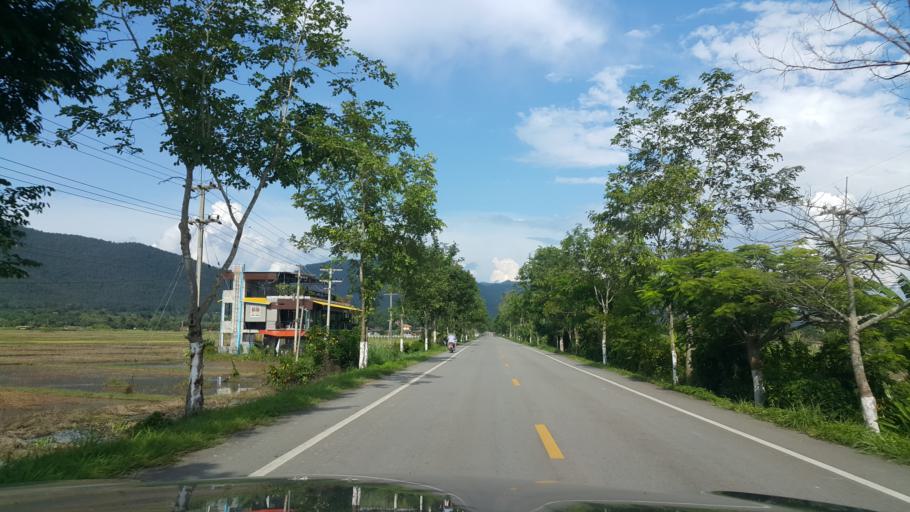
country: TH
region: Chiang Mai
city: Mae Taeng
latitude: 19.1435
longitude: 99.0270
